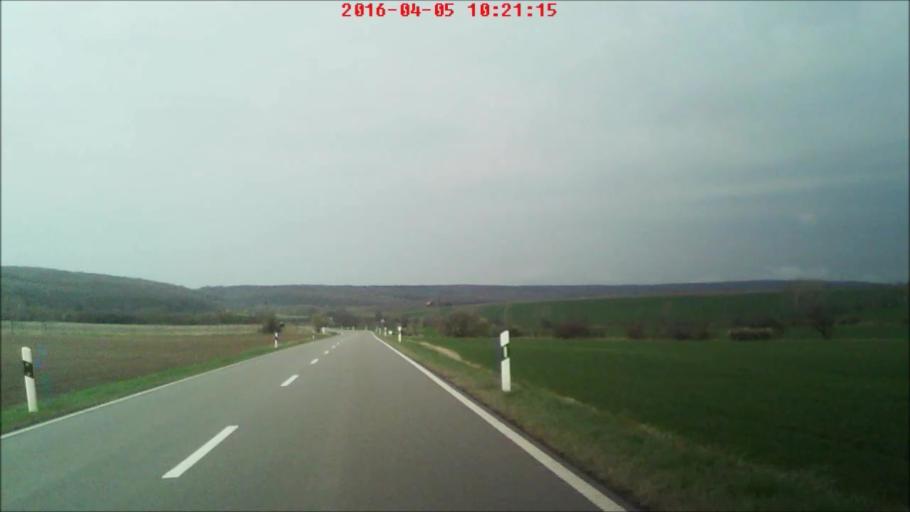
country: DE
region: Thuringia
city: Witterda
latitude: 51.0381
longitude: 10.8807
